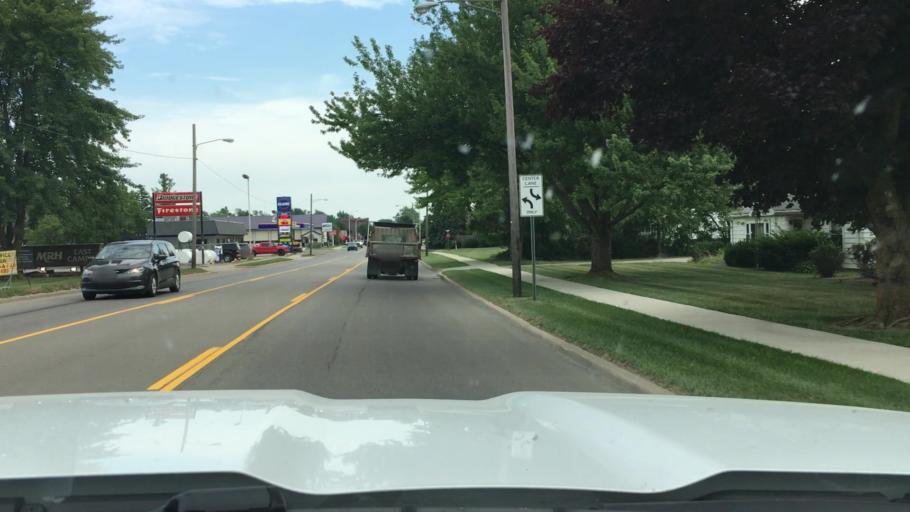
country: US
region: Michigan
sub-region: Sanilac County
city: Marlette
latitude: 43.3315
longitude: -83.0800
